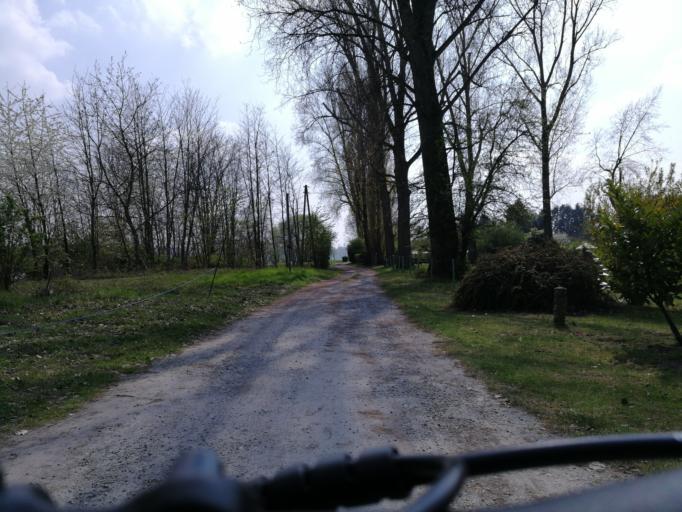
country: DE
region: North Rhine-Westphalia
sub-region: Regierungsbezirk Dusseldorf
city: Dormagen
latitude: 51.1571
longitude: 6.8541
